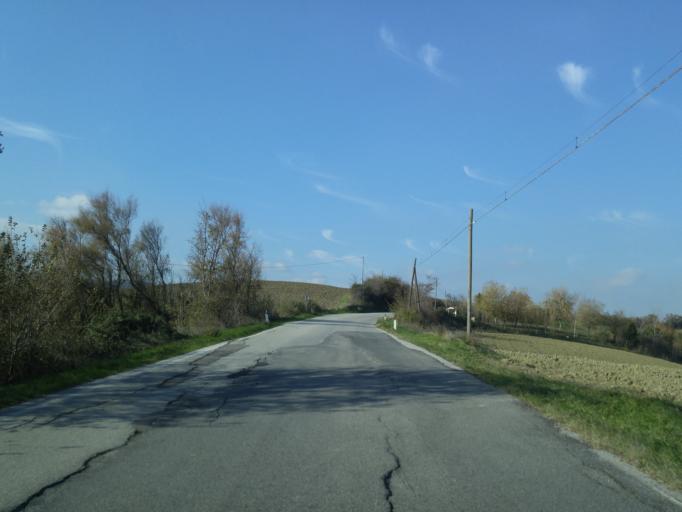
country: IT
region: The Marches
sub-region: Provincia di Pesaro e Urbino
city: Lucrezia
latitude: 43.7964
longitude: 12.9200
